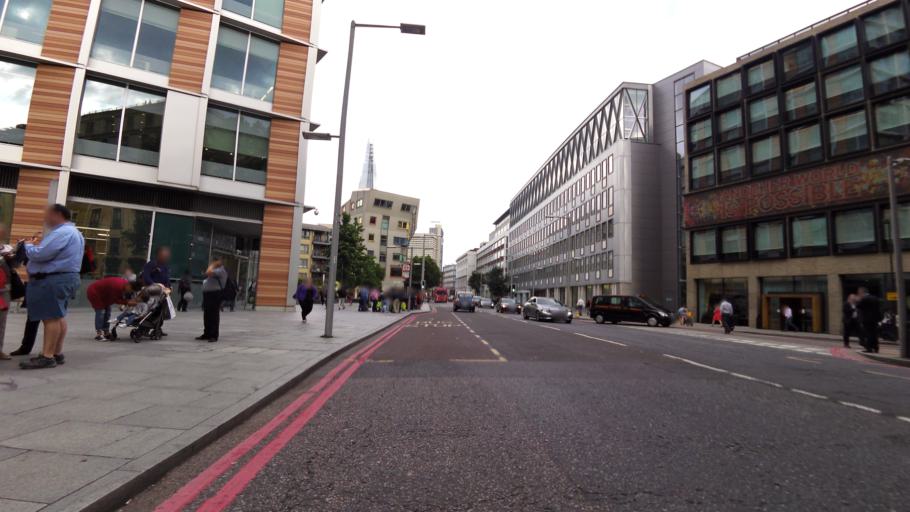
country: GB
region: England
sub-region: Greater London
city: City of London
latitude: 51.5055
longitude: -0.0987
